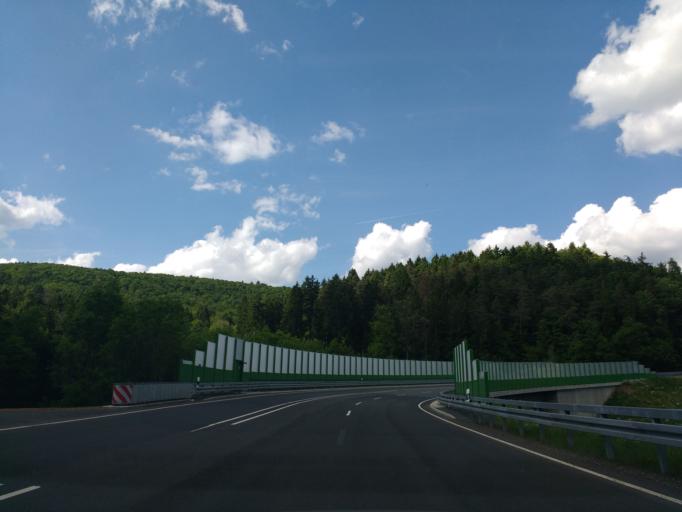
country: DE
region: Hesse
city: Hatzfeld
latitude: 50.9483
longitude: 8.5615
